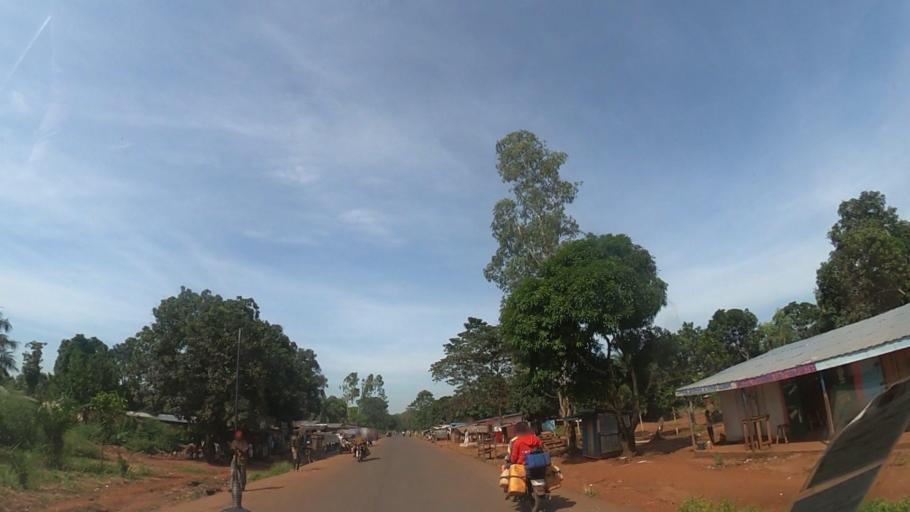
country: CF
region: Bangui
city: Bangui
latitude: 4.3129
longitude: 18.4872
